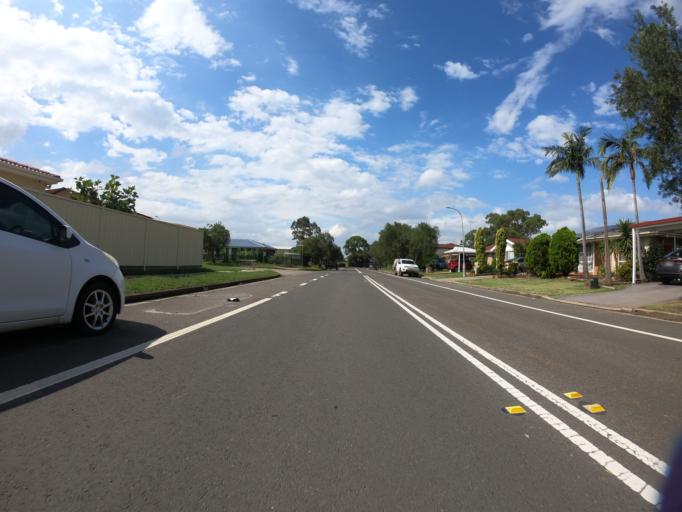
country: AU
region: New South Wales
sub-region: Blacktown
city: Hassall Grove
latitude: -33.7414
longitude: 150.8313
